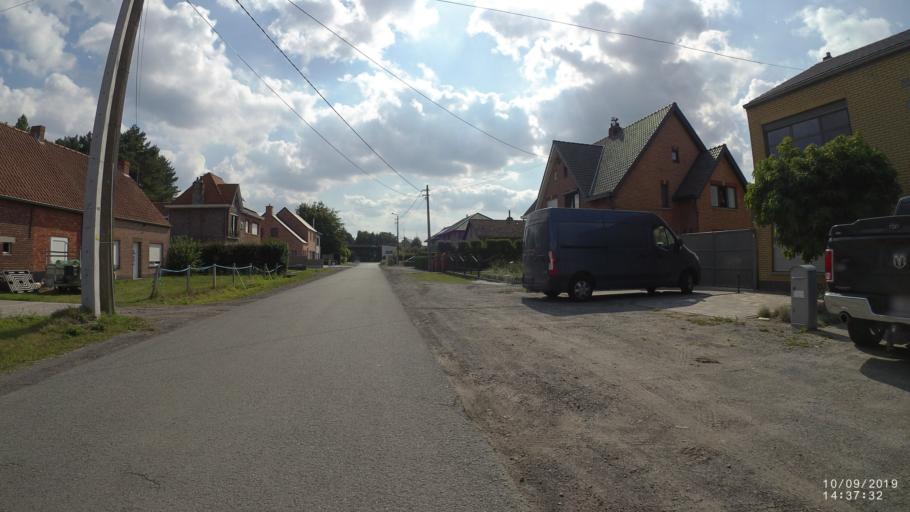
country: BE
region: Flanders
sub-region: Provincie Oost-Vlaanderen
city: Kaprijke
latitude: 51.1888
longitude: 3.6817
